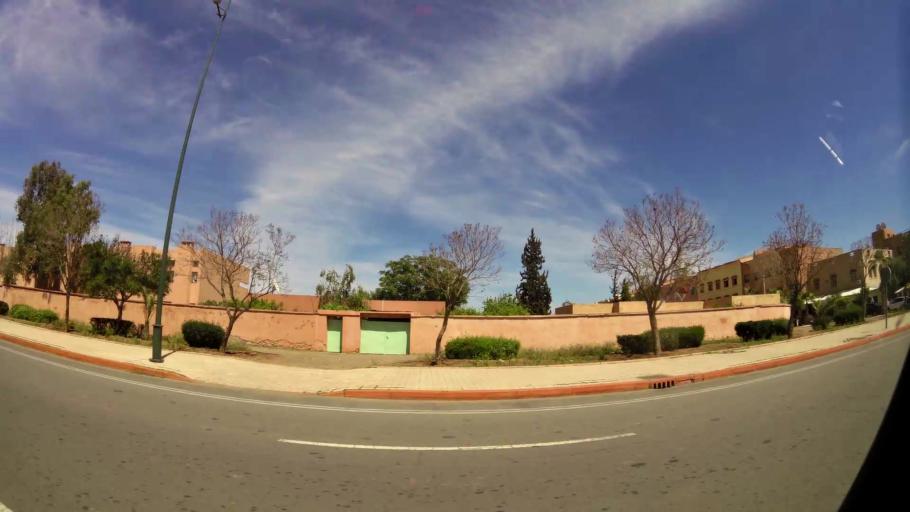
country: MA
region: Marrakech-Tensift-Al Haouz
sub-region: Marrakech
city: Marrakesh
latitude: 31.6085
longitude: -7.9733
